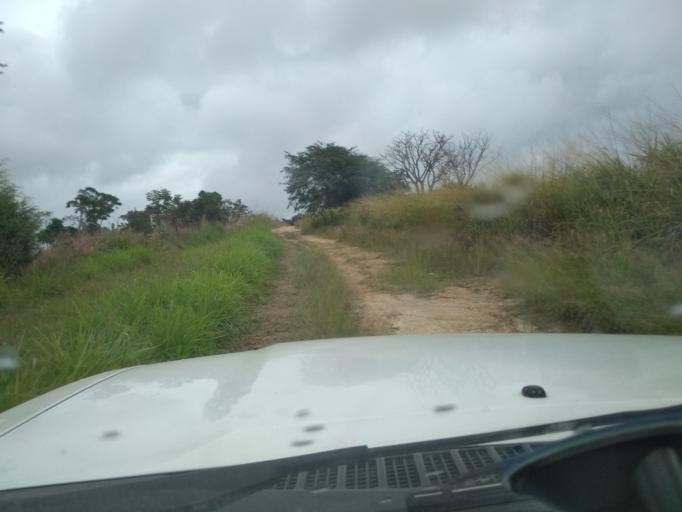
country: MX
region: Veracruz
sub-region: Emiliano Zapata
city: Dos Rios
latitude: 19.5328
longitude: -96.8101
